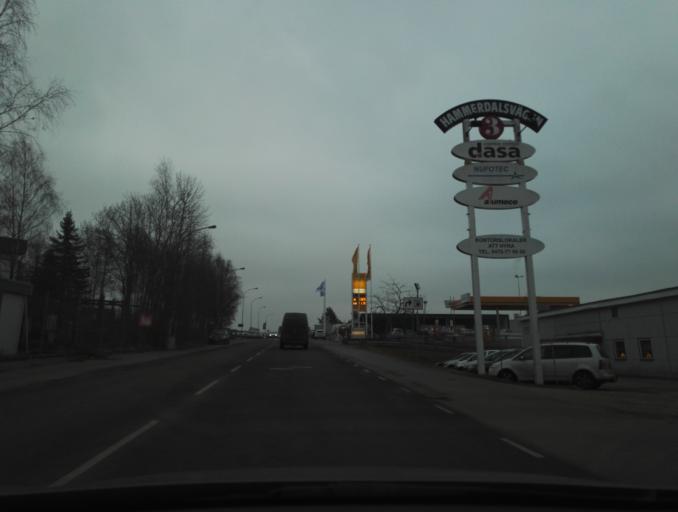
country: SE
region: Kronoberg
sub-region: Vaxjo Kommun
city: Vaexjoe
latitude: 56.8873
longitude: 14.7602
